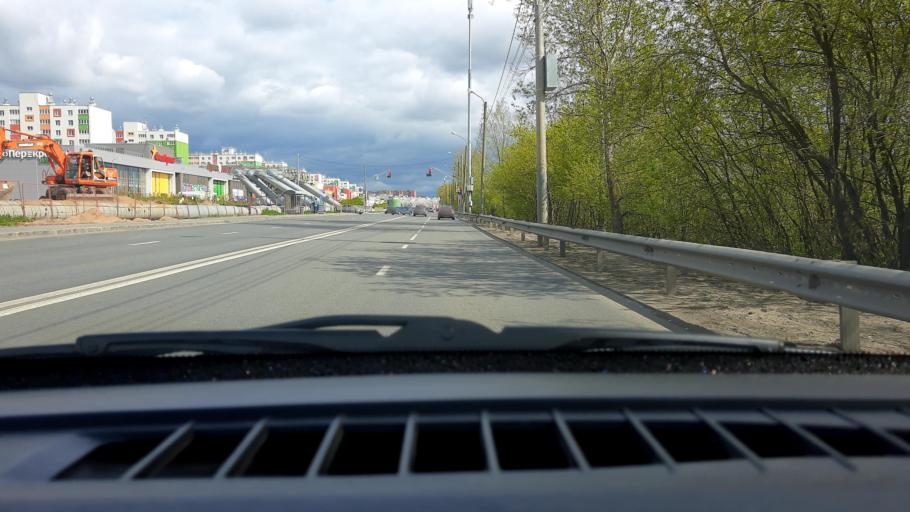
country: RU
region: Nizjnij Novgorod
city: Nizhniy Novgorod
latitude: 56.3417
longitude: 43.9023
